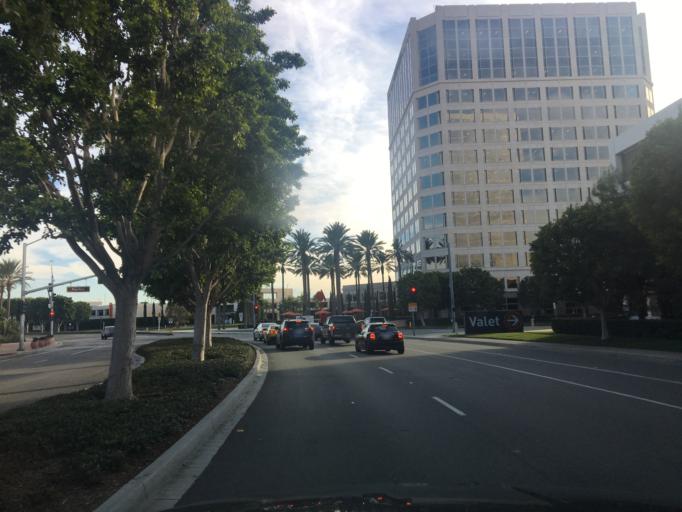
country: US
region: California
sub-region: Orange County
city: Laguna Woods
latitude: 33.6520
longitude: -117.7471
